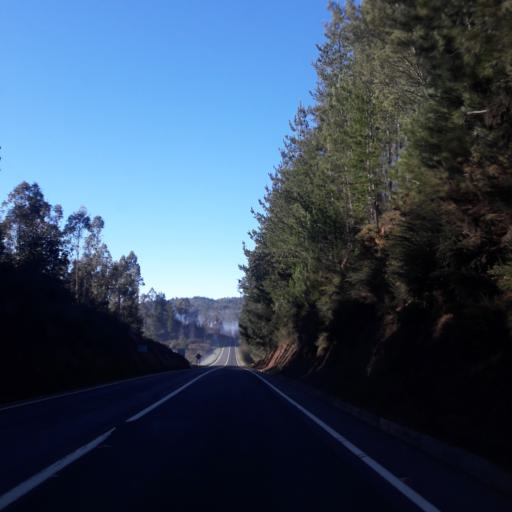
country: CL
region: Biobio
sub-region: Provincia de Biobio
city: La Laja
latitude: -37.2837
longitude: -72.9415
